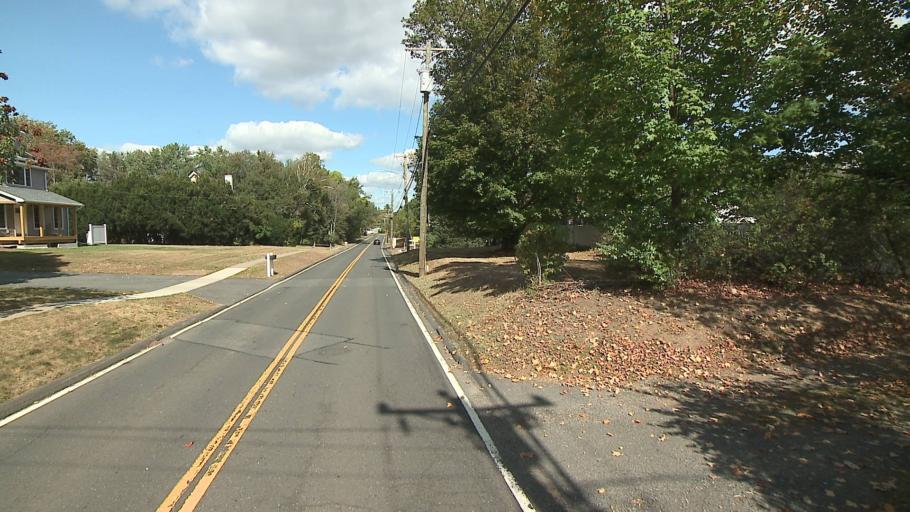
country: US
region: Connecticut
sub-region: New Haven County
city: Cheshire
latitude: 41.4784
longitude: -72.9089
